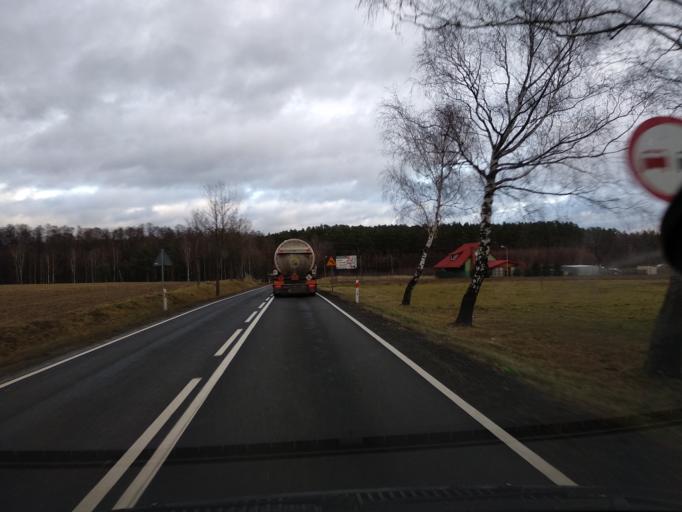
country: PL
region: Lower Silesian Voivodeship
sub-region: Powiat olesnicki
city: Miedzyborz
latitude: 51.3500
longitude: 17.6004
